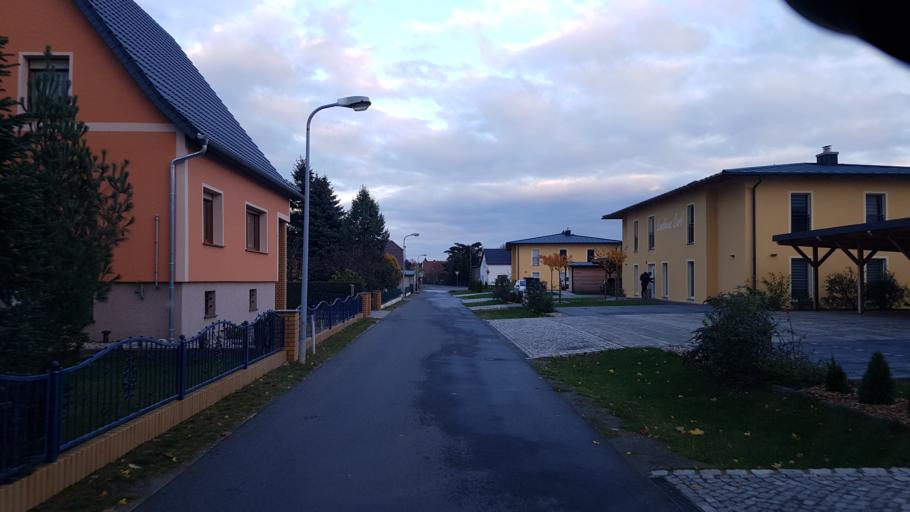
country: DE
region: Brandenburg
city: Lindenau
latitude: 51.4143
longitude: 13.7686
